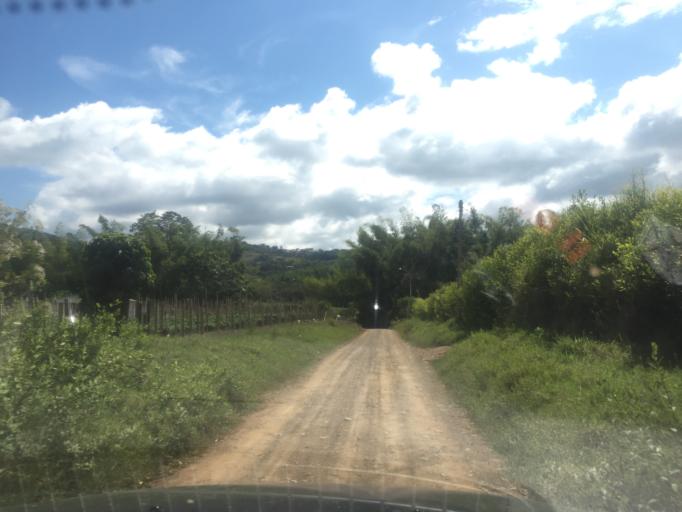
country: CO
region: Valle del Cauca
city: Yumbo
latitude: 3.6656
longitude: -76.5604
